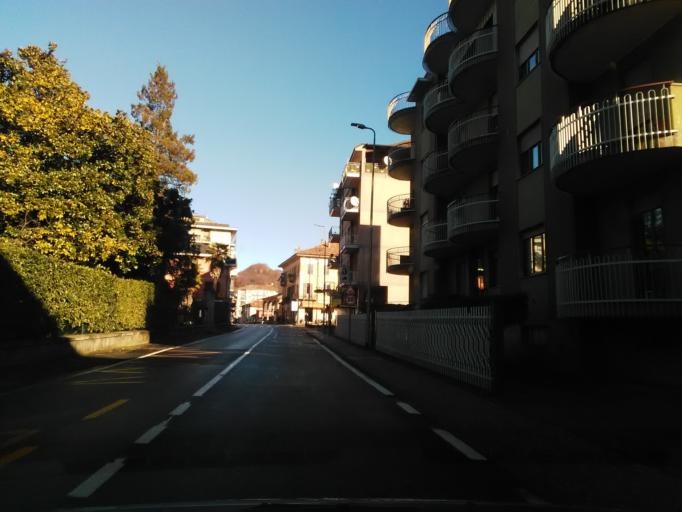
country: IT
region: Piedmont
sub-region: Provincia di Vercelli
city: Quarona
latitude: 45.7591
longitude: 8.2682
